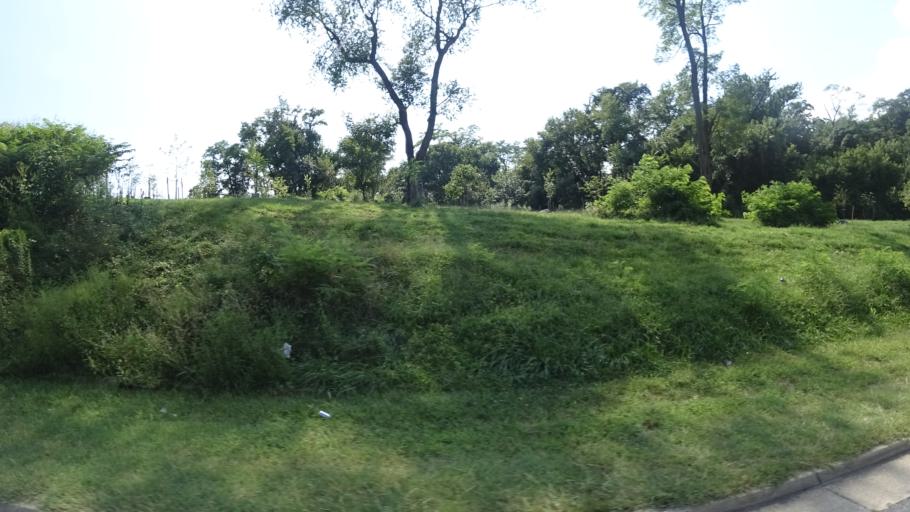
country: US
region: Maryland
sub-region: Prince George's County
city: Hillcrest Heights
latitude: 38.8520
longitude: -76.9738
